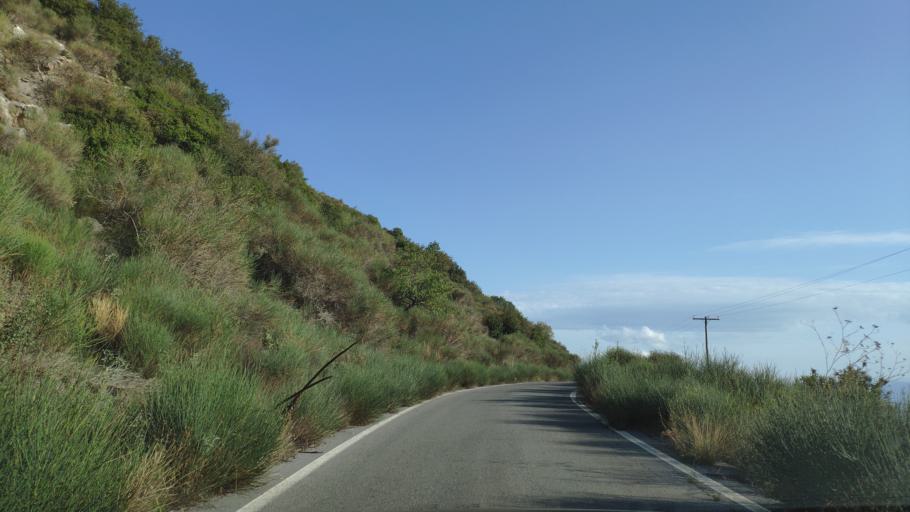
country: GR
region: Peloponnese
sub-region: Nomos Arkadias
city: Dimitsana
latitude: 37.5689
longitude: 22.0218
